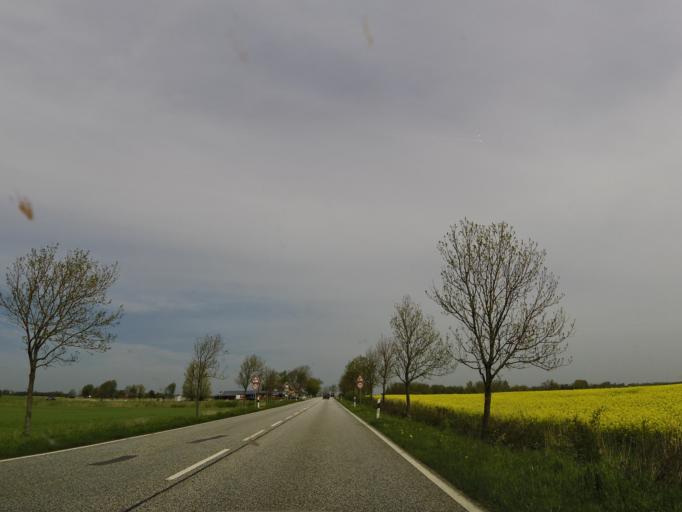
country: DE
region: Schleswig-Holstein
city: Witzwort
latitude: 54.3660
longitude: 8.9778
